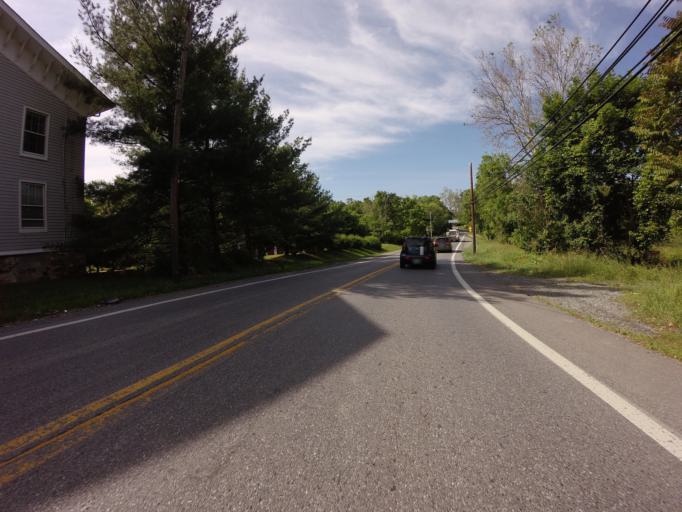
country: US
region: Maryland
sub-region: Frederick County
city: Green Valley
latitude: 39.3716
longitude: -77.2713
